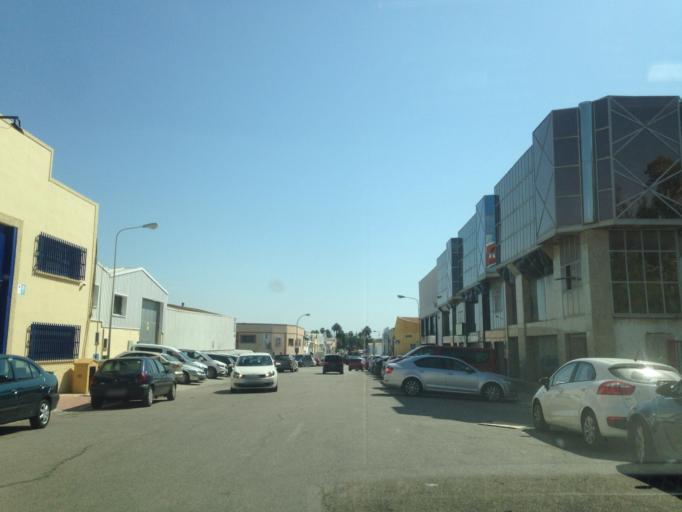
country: ES
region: Andalusia
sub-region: Provincia de Malaga
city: Malaga
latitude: 36.7038
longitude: -4.4776
